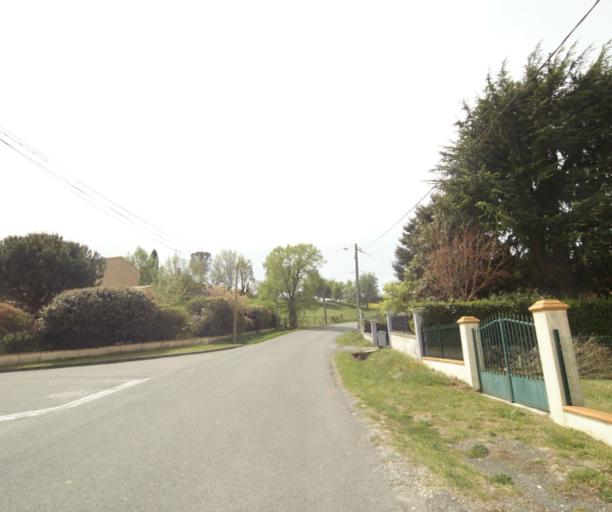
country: FR
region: Midi-Pyrenees
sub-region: Departement de la Haute-Garonne
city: Pompertuzat
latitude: 43.4850
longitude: 1.5113
